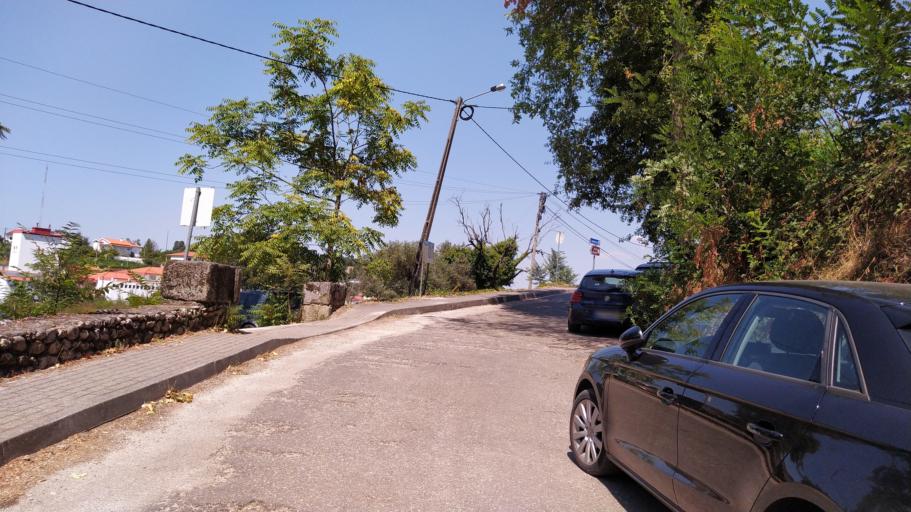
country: PT
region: Coimbra
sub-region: Arganil
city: Arganil
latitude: 40.2669
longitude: -7.9947
